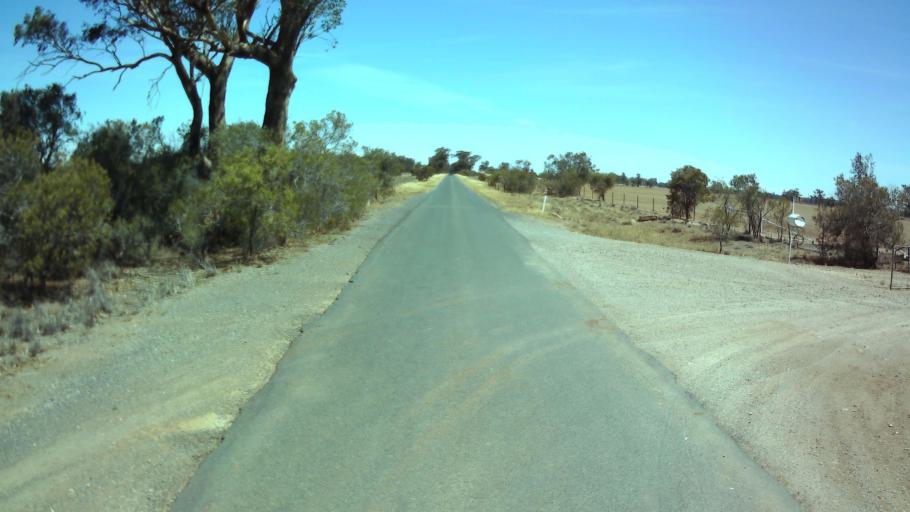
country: AU
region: New South Wales
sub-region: Weddin
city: Grenfell
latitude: -33.8955
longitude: 147.6874
